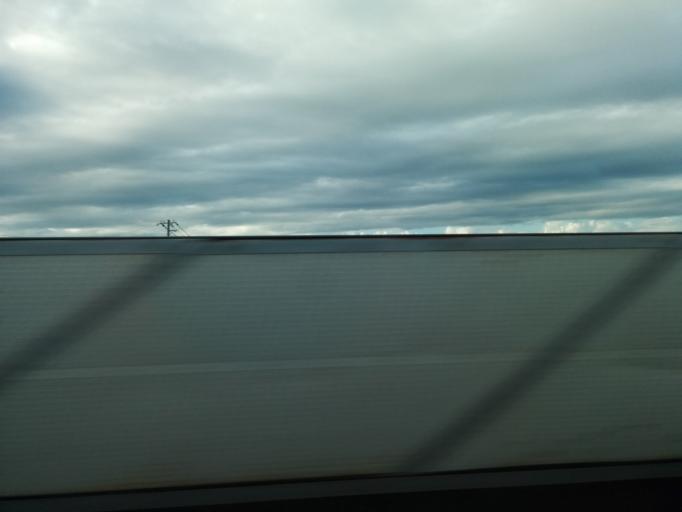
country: JP
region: Shizuoka
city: Fujieda
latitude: 34.8390
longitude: 138.2573
